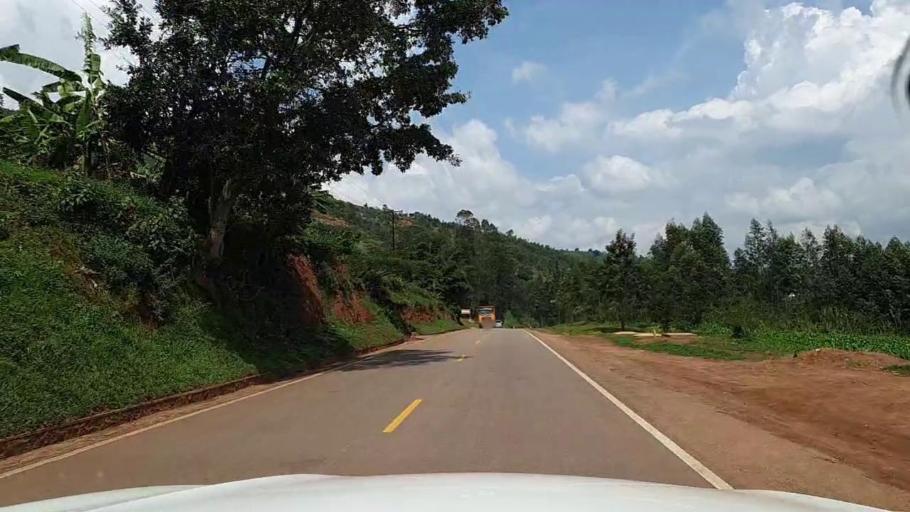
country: RW
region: Kigali
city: Kigali
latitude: -1.8349
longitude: 30.0798
